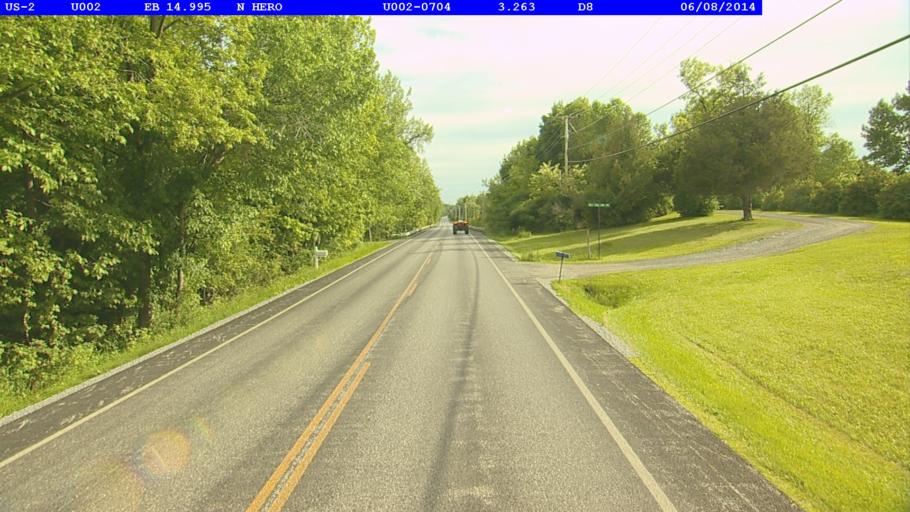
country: US
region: Vermont
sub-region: Grand Isle County
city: North Hero
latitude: 44.8449
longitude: -73.2671
